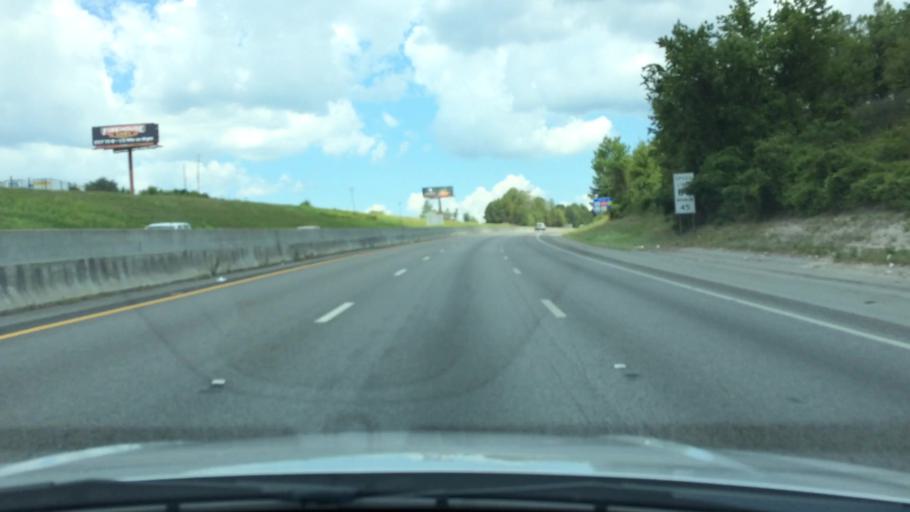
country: US
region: South Carolina
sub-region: Lexington County
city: Springdale
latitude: 33.9400
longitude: -81.0874
